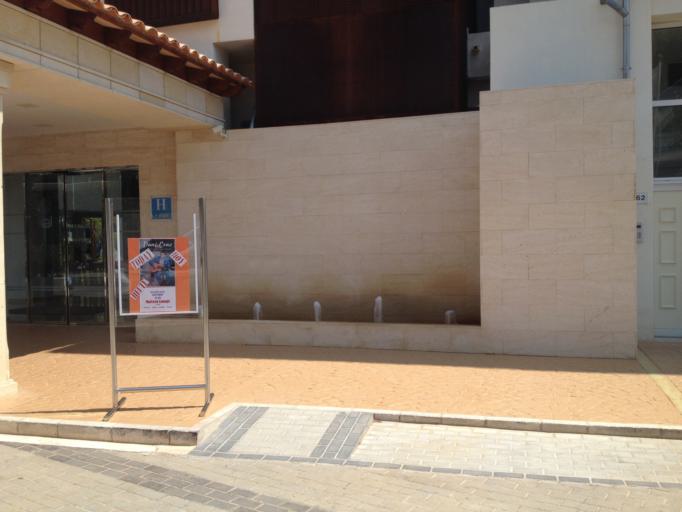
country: ES
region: Balearic Islands
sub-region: Illes Balears
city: Magaluf
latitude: 39.5386
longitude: 2.5921
